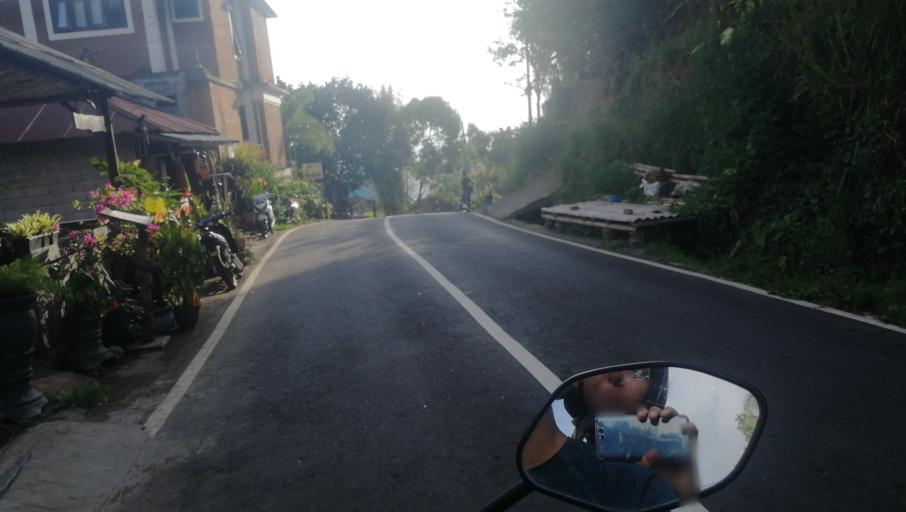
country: ID
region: Bali
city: Munduk
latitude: -8.2650
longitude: 115.0593
